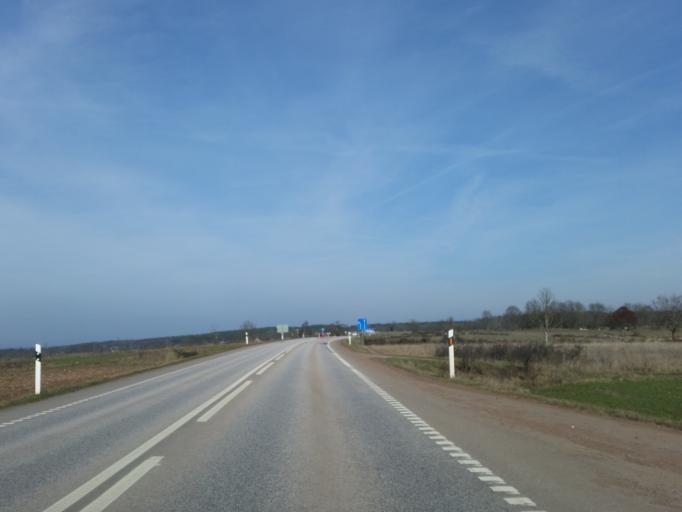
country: SE
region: Kalmar
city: Faerjestaden
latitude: 56.7282
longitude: 16.5394
